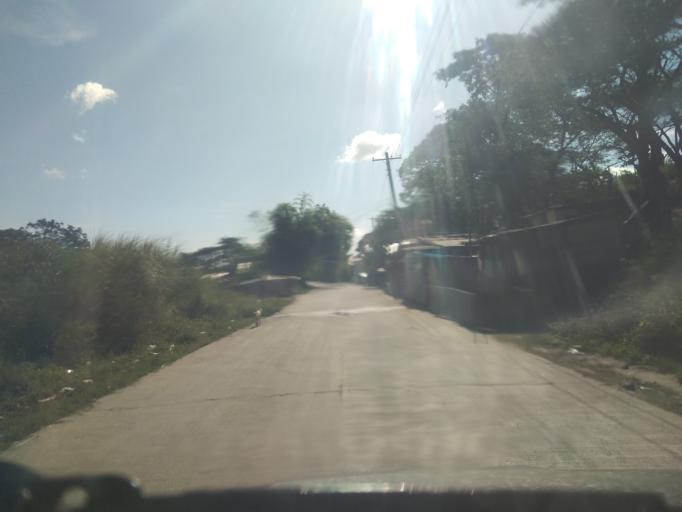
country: PH
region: Central Luzon
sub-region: Province of Pampanga
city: Calibutbut
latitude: 15.0880
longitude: 120.6017
